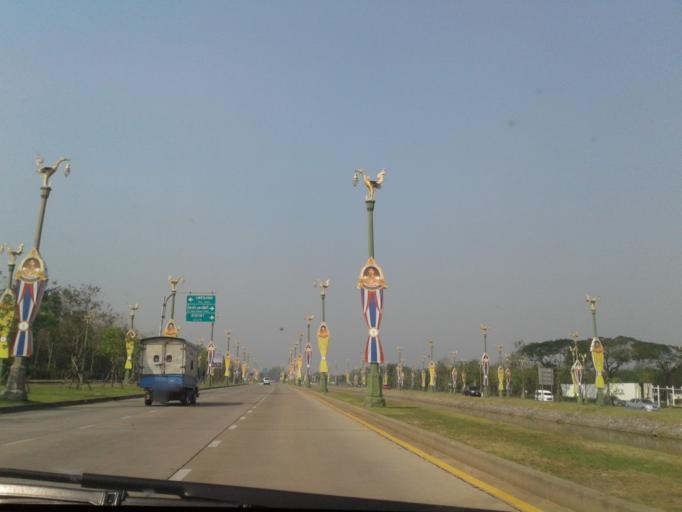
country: TH
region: Bangkok
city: Thawi Watthana
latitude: 13.7771
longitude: 100.3330
